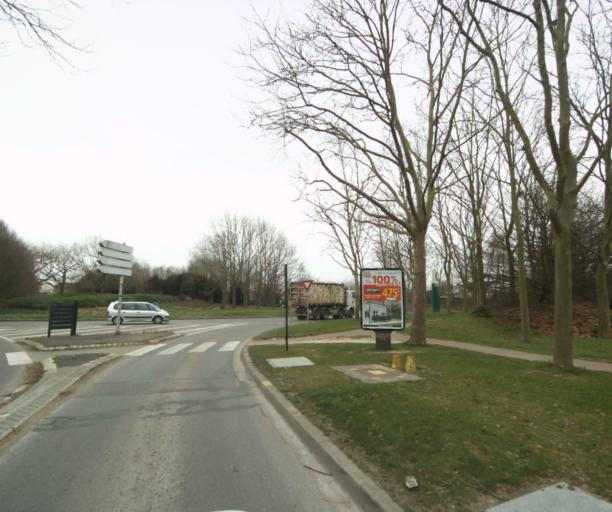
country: FR
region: Ile-de-France
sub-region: Departement du Val-d'Oise
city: Vaureal
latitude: 49.0466
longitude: 2.0238
